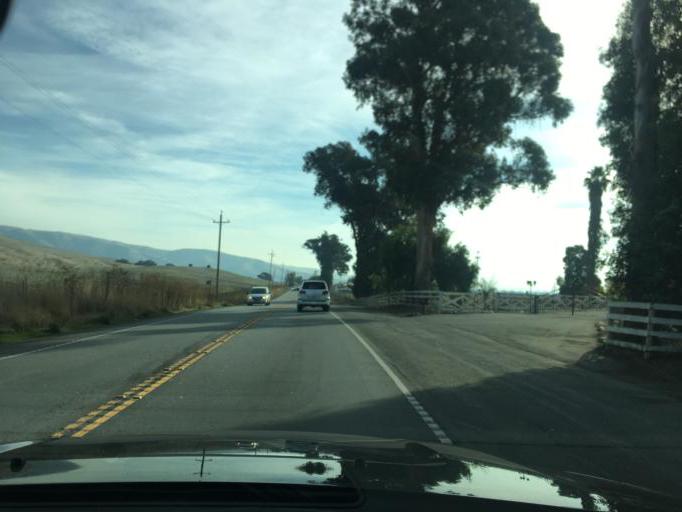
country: US
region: California
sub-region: Santa Clara County
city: Gilroy
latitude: 36.9846
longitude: -121.4786
